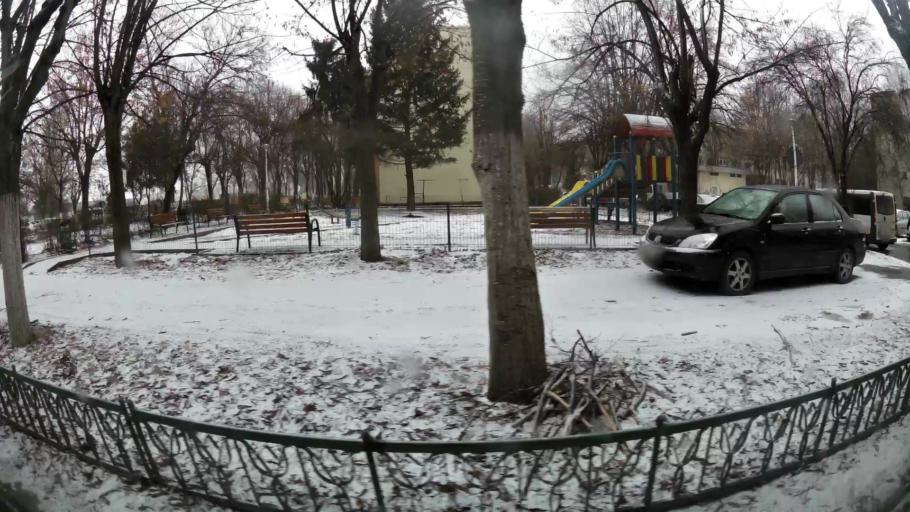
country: RO
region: Prahova
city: Ploiesti
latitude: 44.9618
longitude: 26.0080
